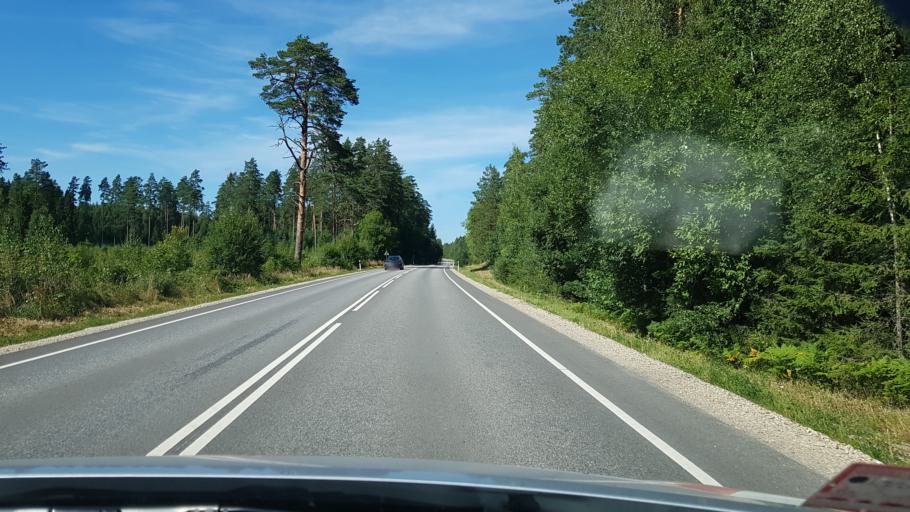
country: EE
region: Polvamaa
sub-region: Polva linn
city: Polva
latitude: 58.0155
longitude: 27.1703
